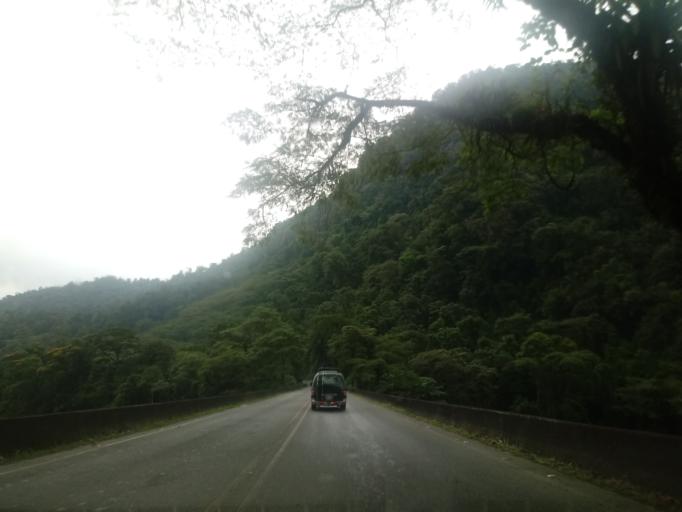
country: CR
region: San Jose
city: Dulce Nombre de Jesus
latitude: 10.1472
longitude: -83.9480
